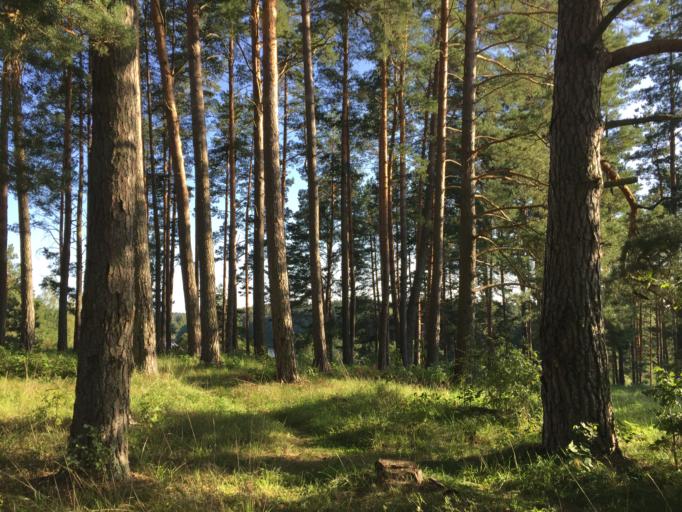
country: LT
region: Panevezys
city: Rokiskis
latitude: 55.8270
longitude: 25.8687
